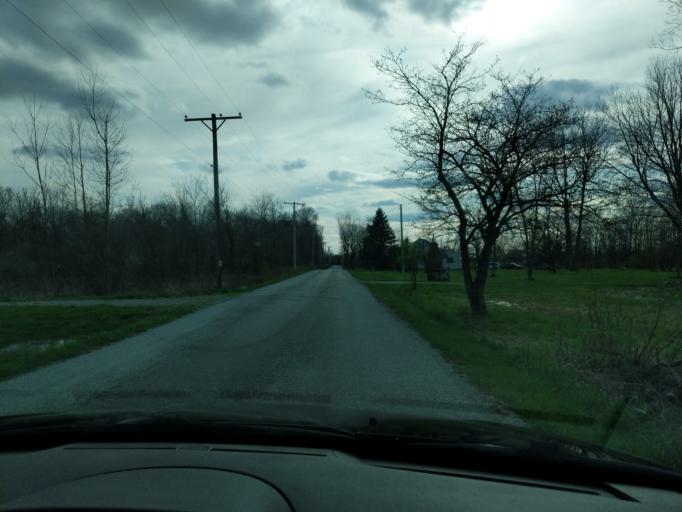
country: US
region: Ohio
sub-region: Champaign County
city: Urbana
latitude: 40.1322
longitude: -83.6591
